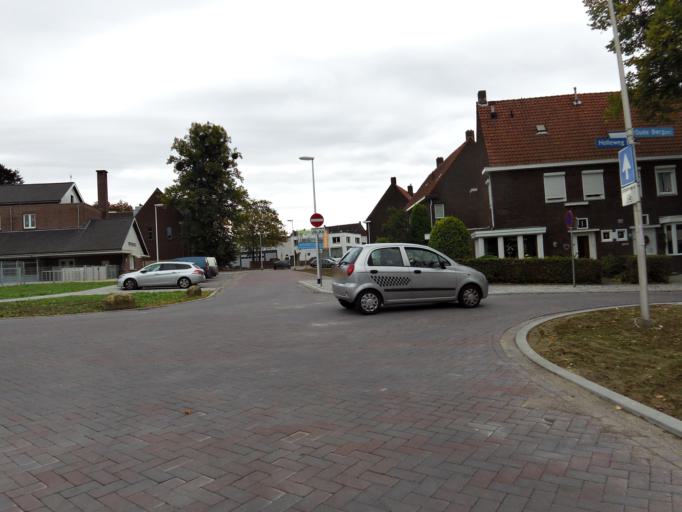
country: NL
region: Limburg
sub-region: Gemeente Heerlen
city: Heerlen
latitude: 50.8852
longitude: 5.9928
